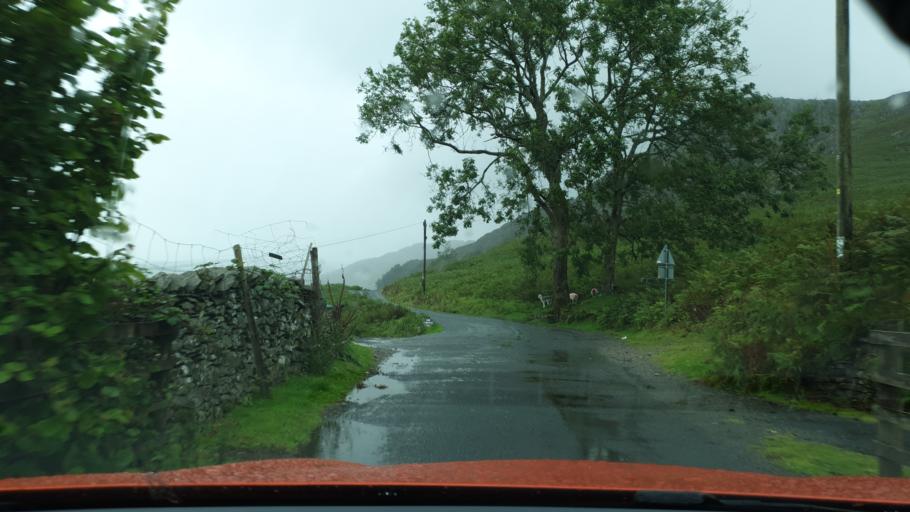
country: GB
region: England
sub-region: Cumbria
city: Millom
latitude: 54.3028
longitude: -3.2283
